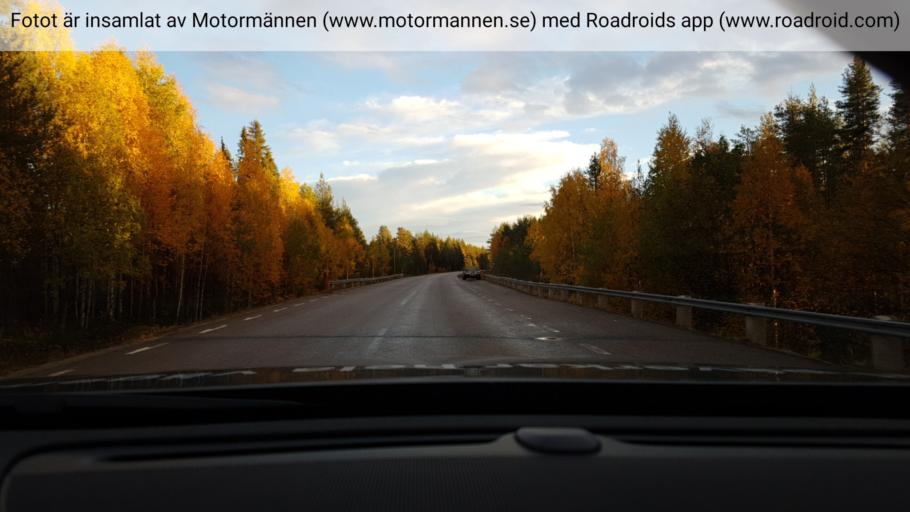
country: SE
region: Norrbotten
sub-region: Overkalix Kommun
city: OEverkalix
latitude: 66.6202
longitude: 22.7475
